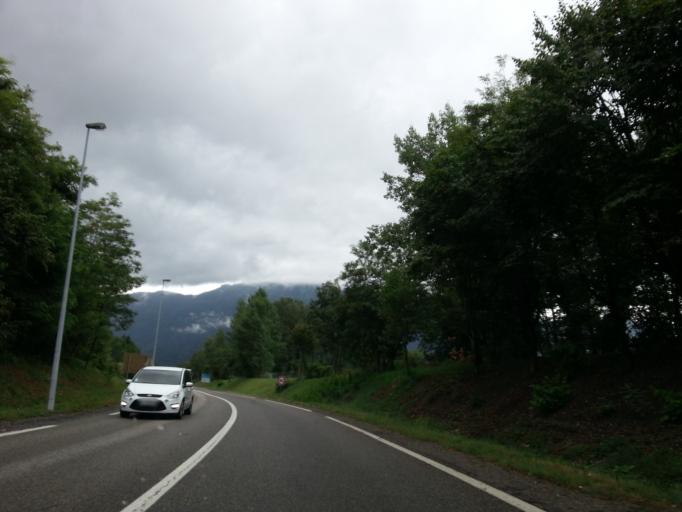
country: FR
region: Rhone-Alpes
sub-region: Departement de la Haute-Savoie
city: Faverges
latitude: 45.7563
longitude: 6.2732
